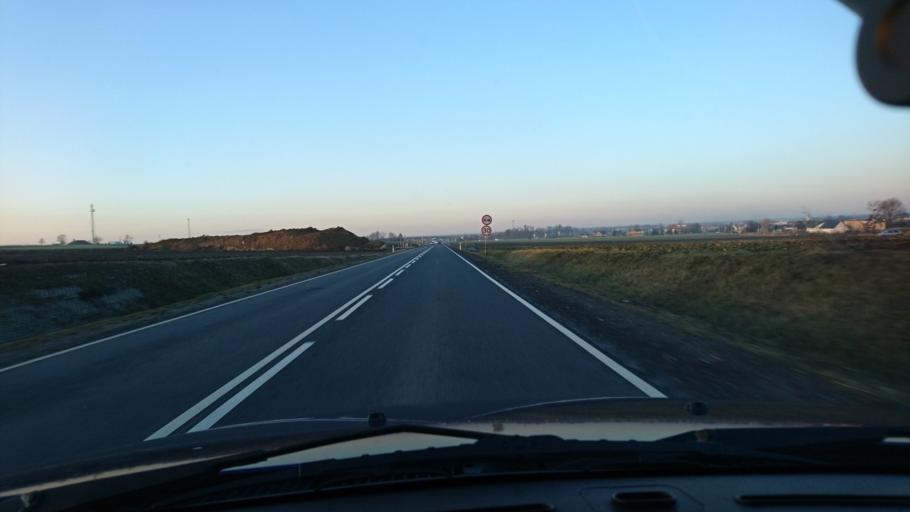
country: PL
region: Silesian Voivodeship
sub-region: Powiat gliwicki
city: Wielowies
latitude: 50.4952
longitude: 18.6072
